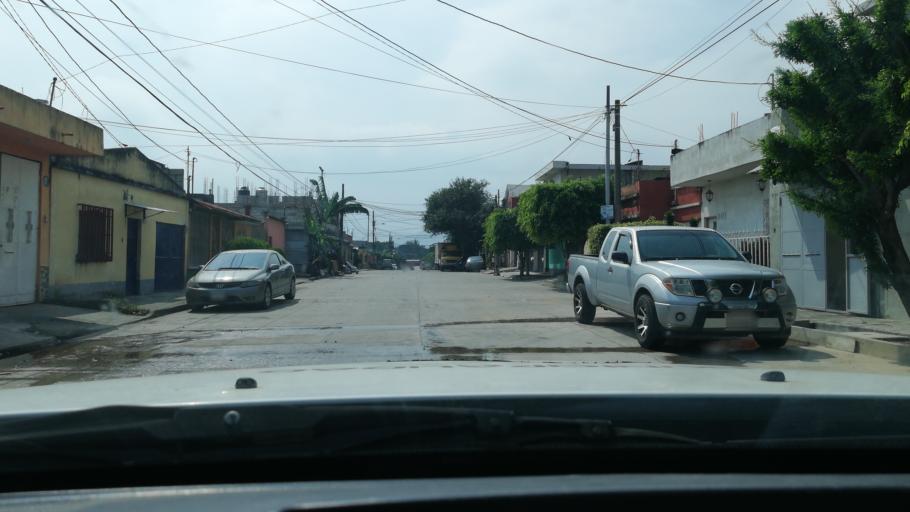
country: GT
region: Guatemala
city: Petapa
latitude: 14.5090
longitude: -90.5664
